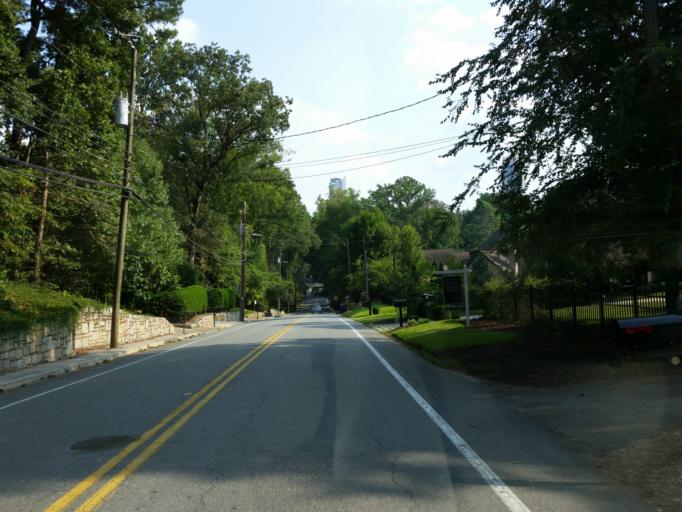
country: US
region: Georgia
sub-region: DeKalb County
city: North Atlanta
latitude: 33.8671
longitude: -84.3579
